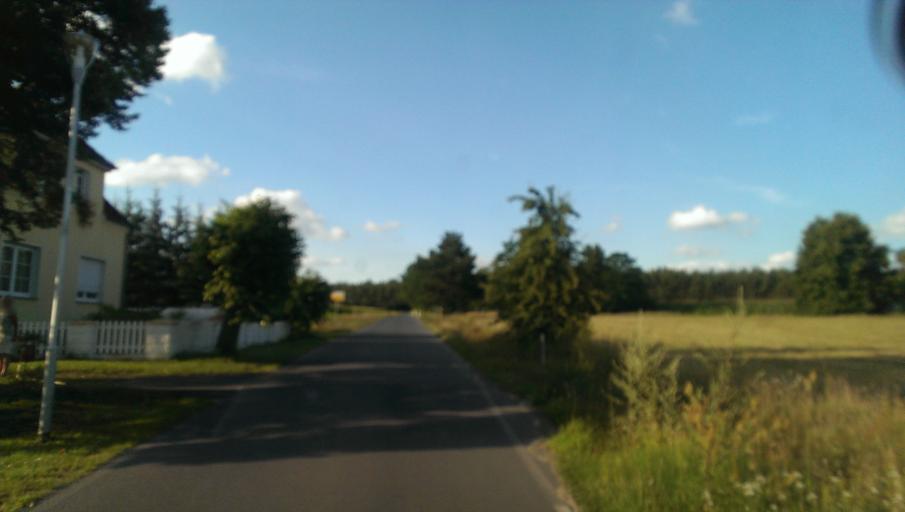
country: DE
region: Brandenburg
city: Treuenbrietzen
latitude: 52.0402
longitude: 12.8660
